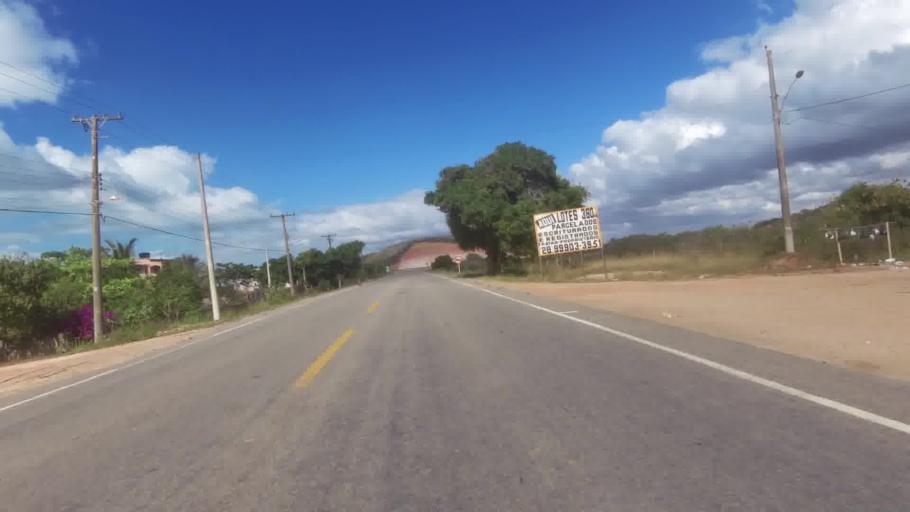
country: BR
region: Espirito Santo
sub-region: Marataizes
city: Marataizes
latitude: -21.1825
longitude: -40.9241
